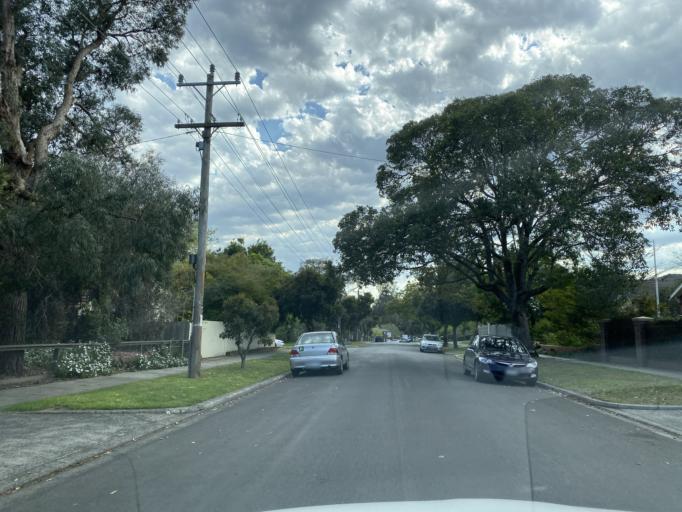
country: AU
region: Victoria
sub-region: Boroondara
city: Camberwell
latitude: -37.8356
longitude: 145.0791
